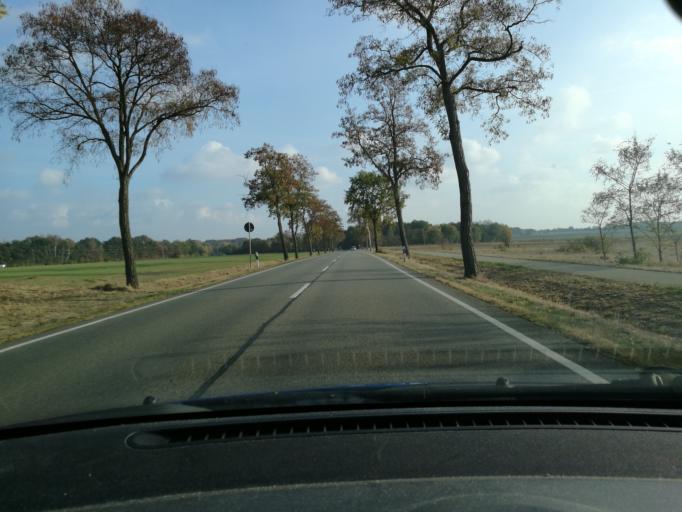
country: DE
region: Lower Saxony
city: Kusten
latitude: 52.9962
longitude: 11.1110
